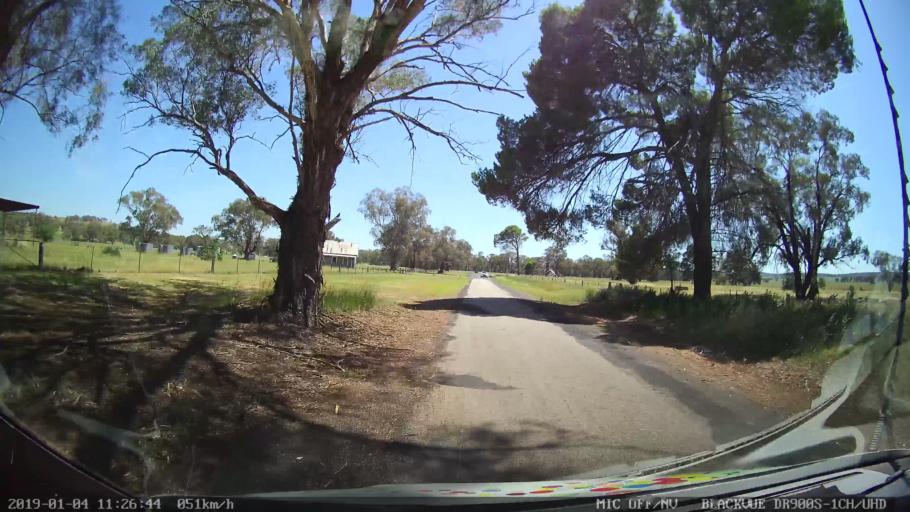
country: AU
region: New South Wales
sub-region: Cabonne
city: Molong
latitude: -33.1133
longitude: 148.7571
